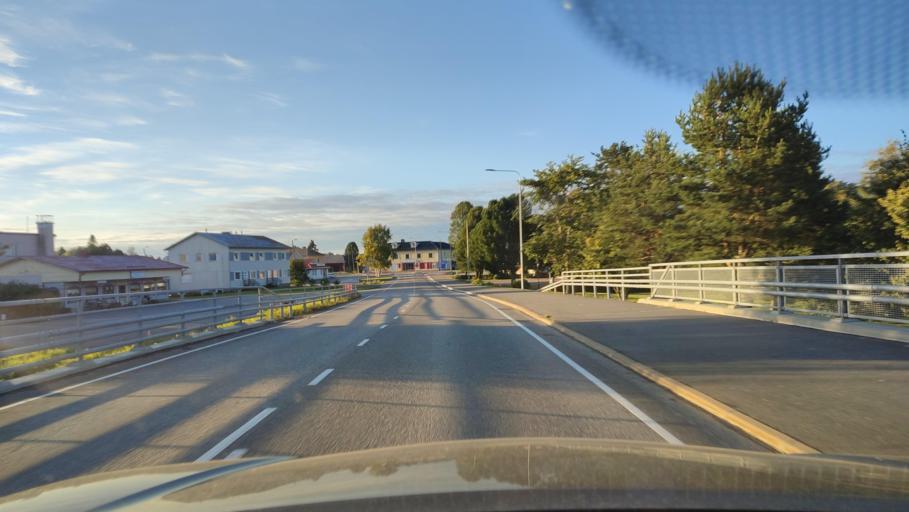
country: FI
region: Ostrobothnia
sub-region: Sydosterbotten
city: Kristinestad
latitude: 62.2531
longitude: 21.5098
